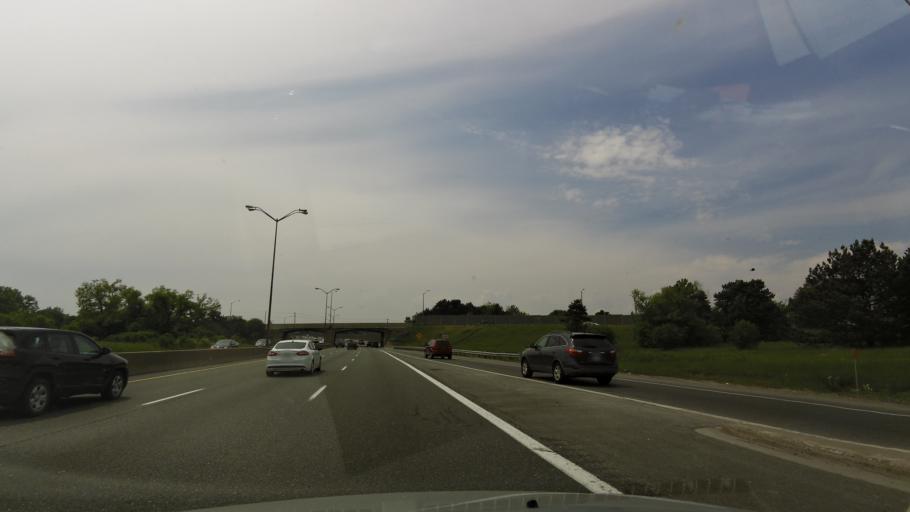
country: CA
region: Ontario
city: Oshawa
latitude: 43.8872
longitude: -78.8274
